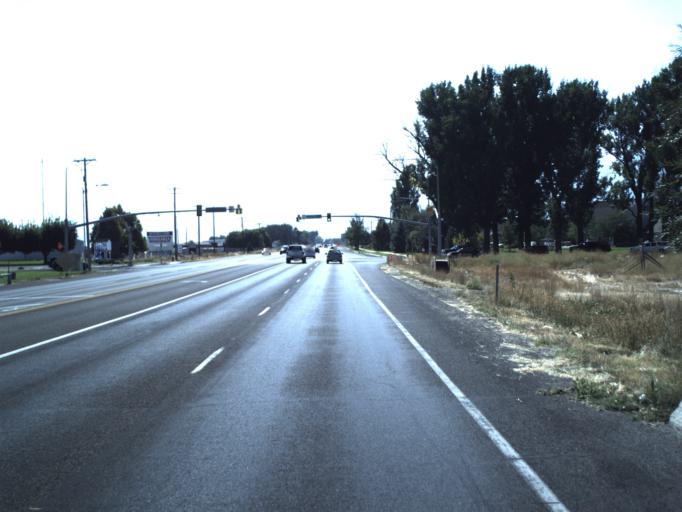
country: US
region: Utah
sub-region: Cache County
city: Providence
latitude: 41.7043
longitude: -111.8506
